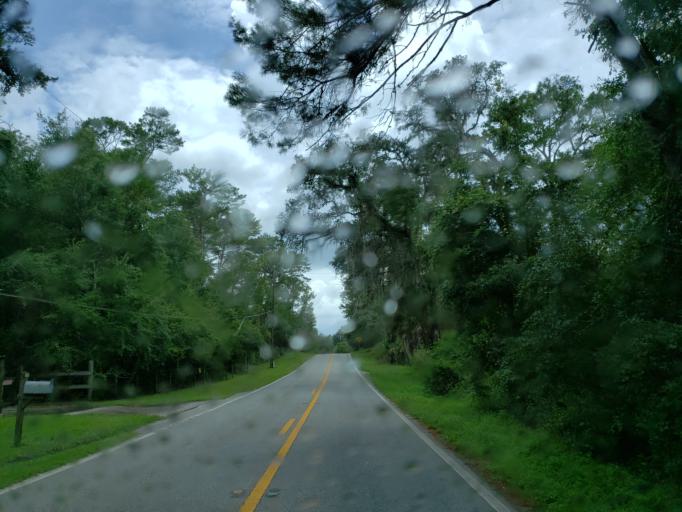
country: US
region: Florida
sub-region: Citrus County
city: Floral City
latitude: 28.6576
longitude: -82.3148
